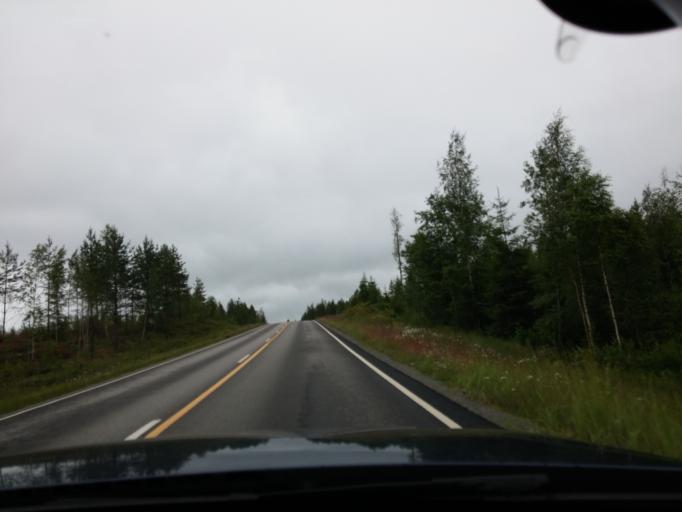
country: FI
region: Central Finland
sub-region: Saarijaervi-Viitasaari
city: Pylkoenmaeki
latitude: 62.6407
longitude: 24.8473
